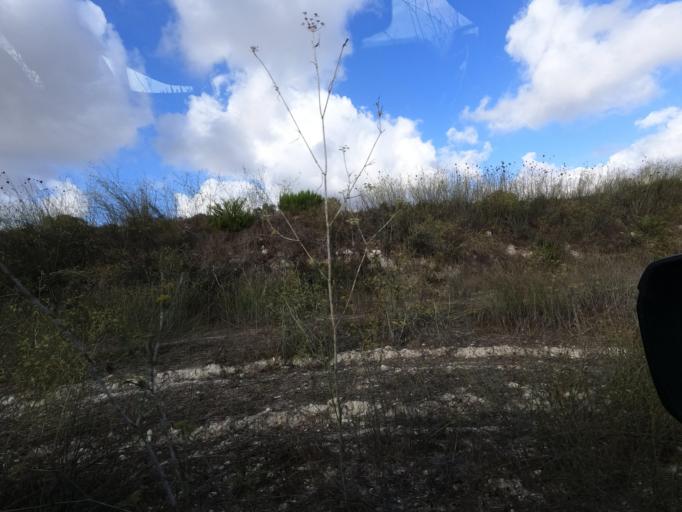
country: CY
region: Pafos
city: Mesogi
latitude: 34.8378
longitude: 32.4860
